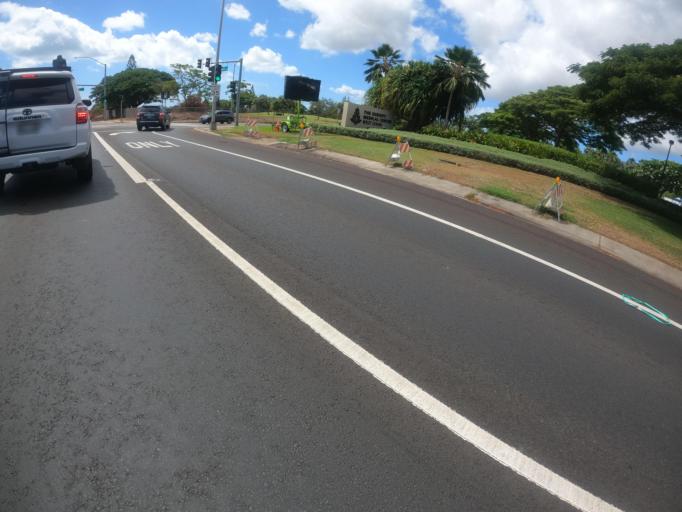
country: US
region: Hawaii
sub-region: Honolulu County
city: Waipahu
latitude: 21.3701
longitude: -158.0263
